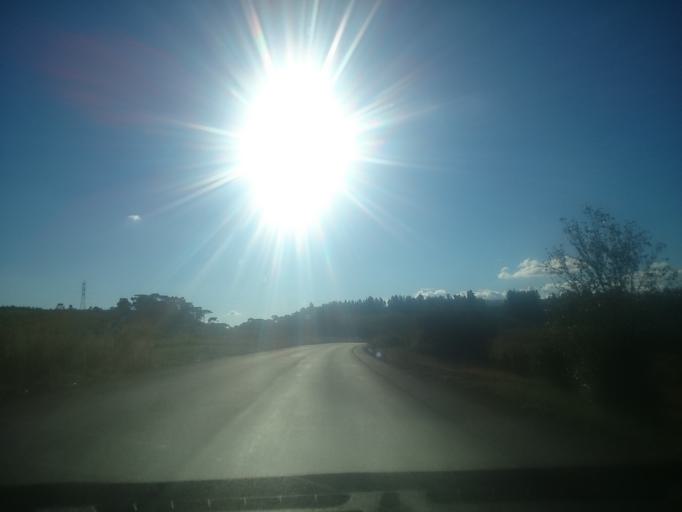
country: BR
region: Santa Catarina
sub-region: Sao Joaquim
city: Sao Joaquim
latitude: -28.1898
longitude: -50.0002
